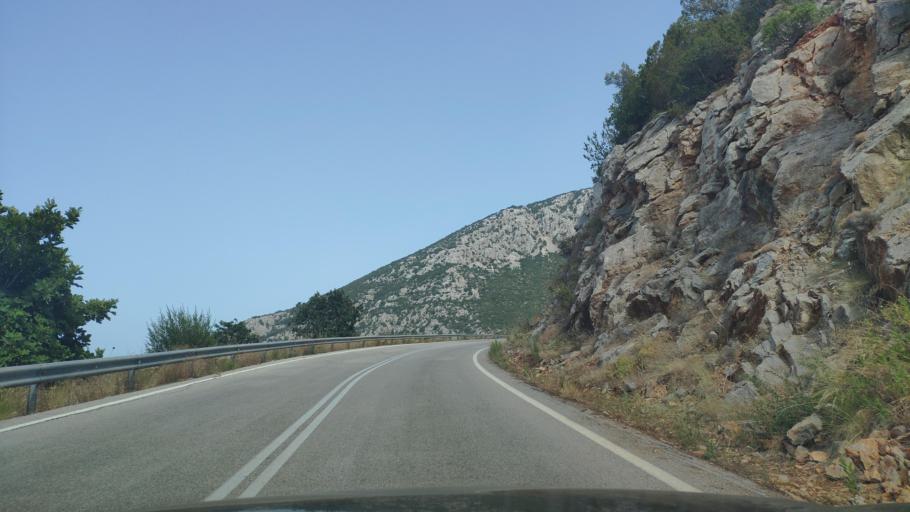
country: GR
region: Peloponnese
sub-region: Nomos Argolidos
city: Palaia Epidavros
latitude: 37.6059
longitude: 23.1574
